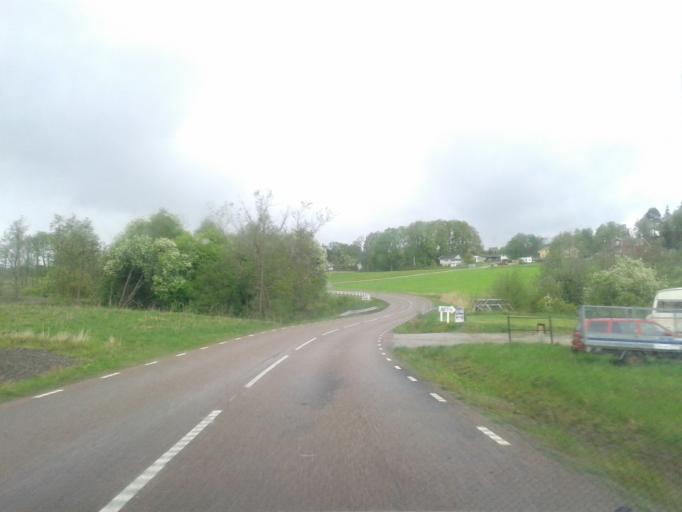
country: SE
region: Vaestra Goetaland
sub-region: Lilla Edets Kommun
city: Lilla Edet
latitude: 58.1157
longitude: 12.1149
